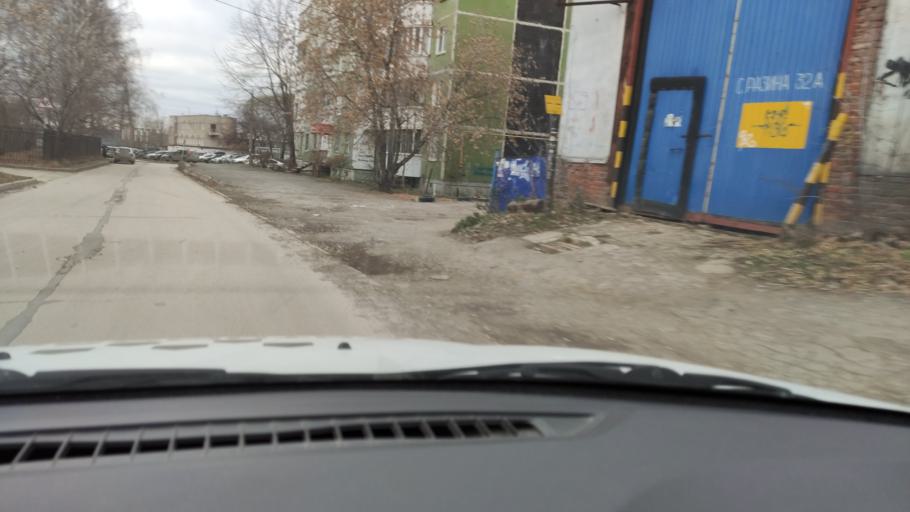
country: RU
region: Perm
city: Perm
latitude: 58.0222
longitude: 56.2728
